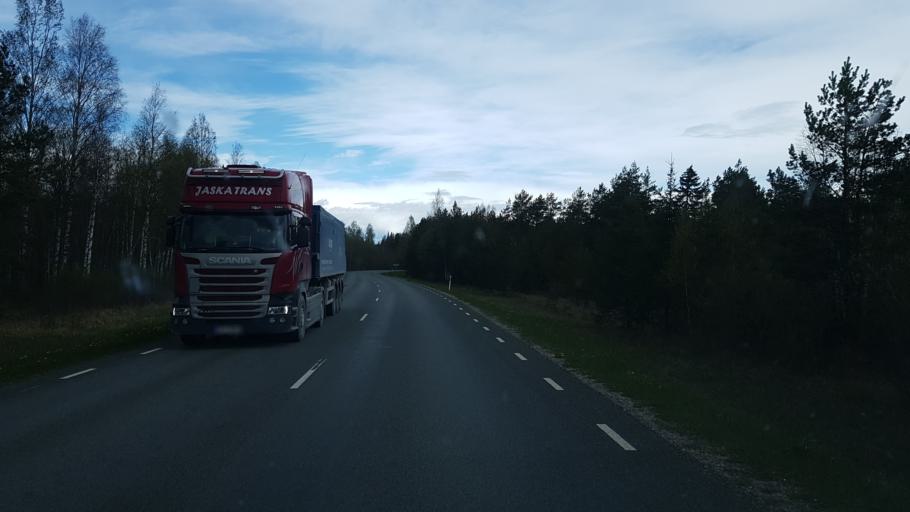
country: EE
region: Laeaene
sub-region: Lihula vald
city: Lihula
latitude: 58.5954
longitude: 23.9697
